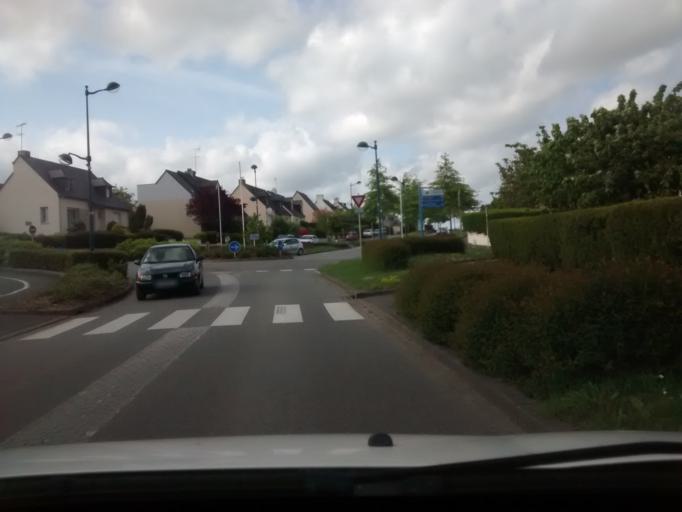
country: FR
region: Brittany
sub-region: Departement d'Ille-et-Vilaine
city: Chateaugiron
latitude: 48.0592
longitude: -1.5246
